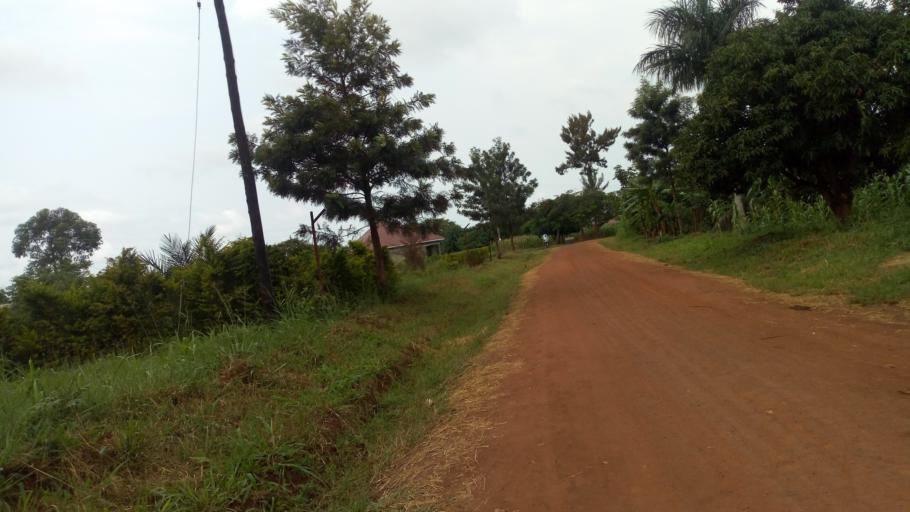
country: UG
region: Western Region
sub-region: Kiryandongo District
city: Kiryandongo
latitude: 1.7988
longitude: 32.0083
